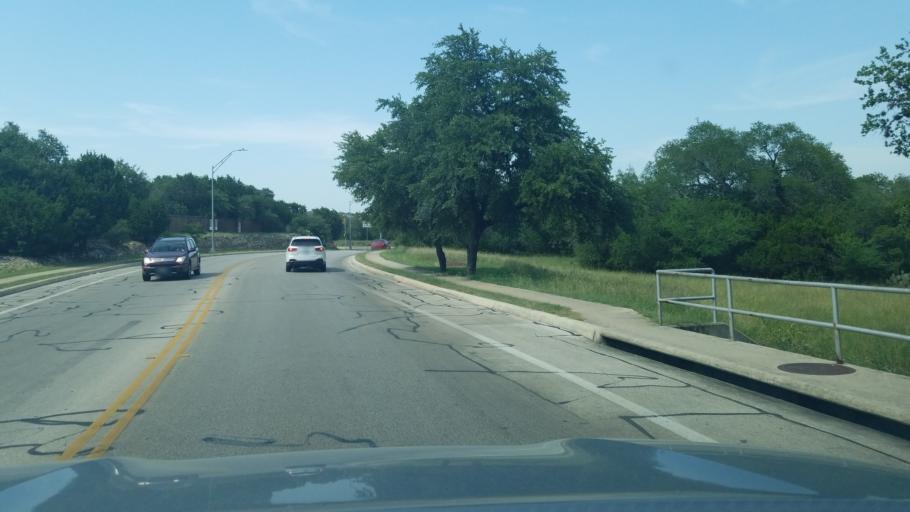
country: US
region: Texas
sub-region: Bexar County
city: Hollywood Park
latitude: 29.6384
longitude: -98.4799
